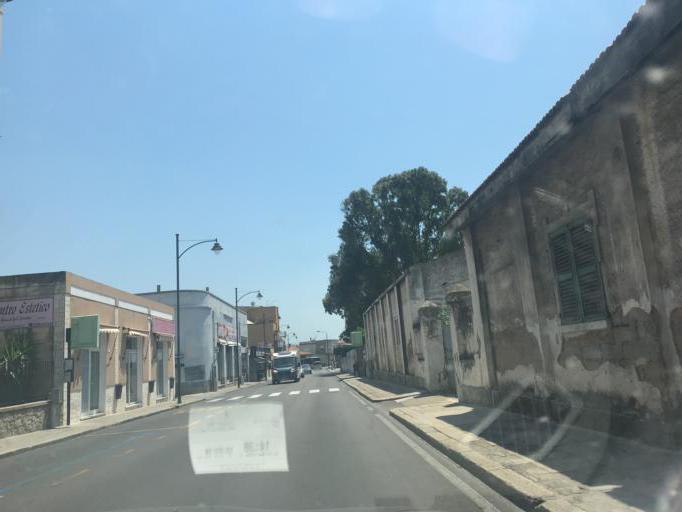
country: IT
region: Sardinia
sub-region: Provincia di Olbia-Tempio
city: Olbia
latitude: 40.9213
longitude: 9.4970
